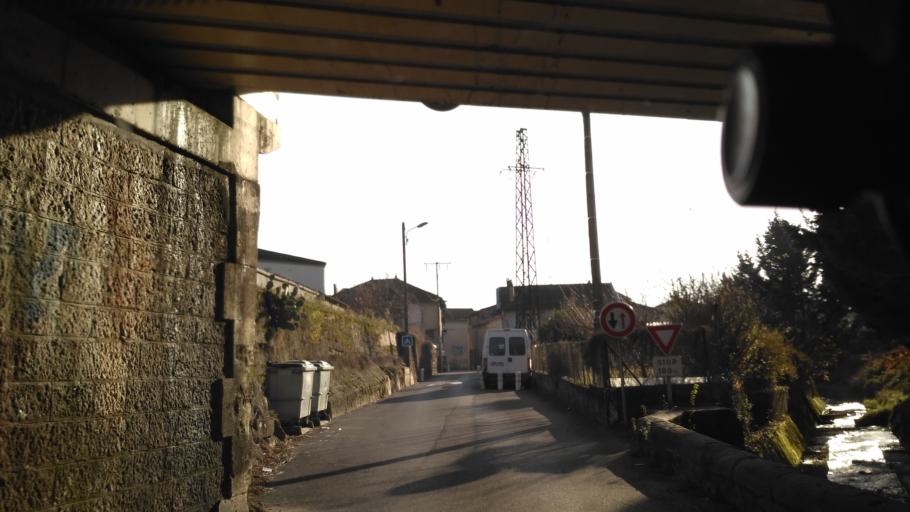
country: FR
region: Rhone-Alpes
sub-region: Departement de la Drome
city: Saint-Paul-les-Romans
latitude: 45.0713
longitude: 5.1332
